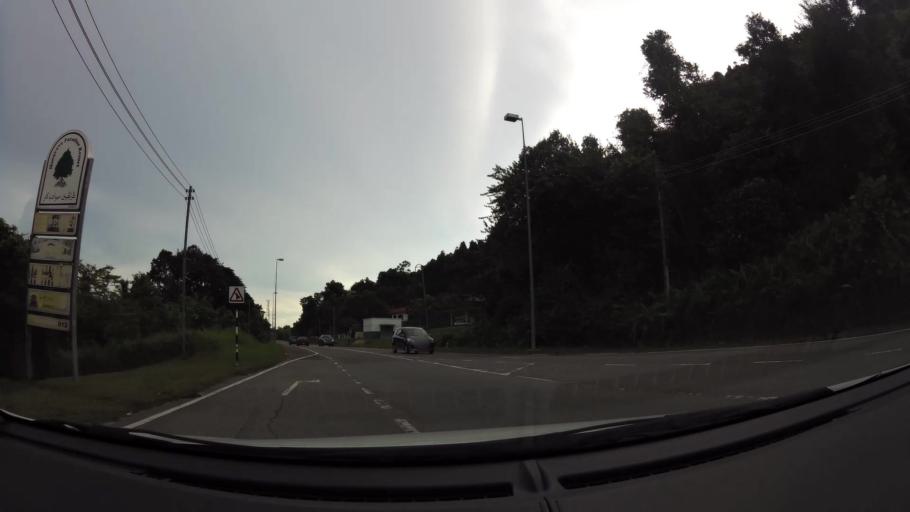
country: BN
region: Brunei and Muara
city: Bandar Seri Begawan
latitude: 4.9129
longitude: 115.0021
